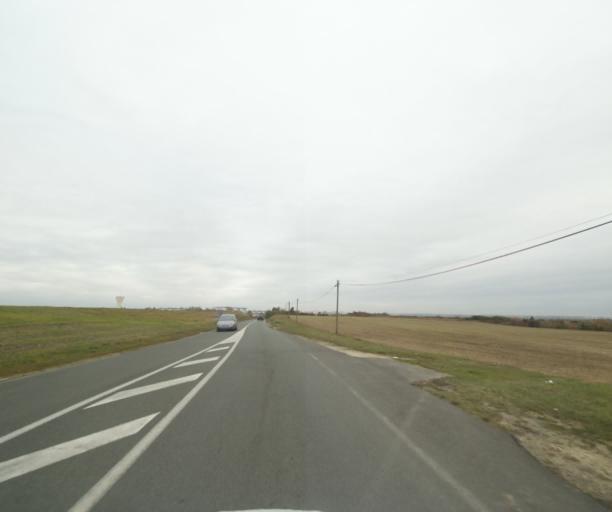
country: FR
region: Poitou-Charentes
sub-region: Departement de la Charente-Maritime
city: Saintes
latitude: 45.7217
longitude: -0.6560
